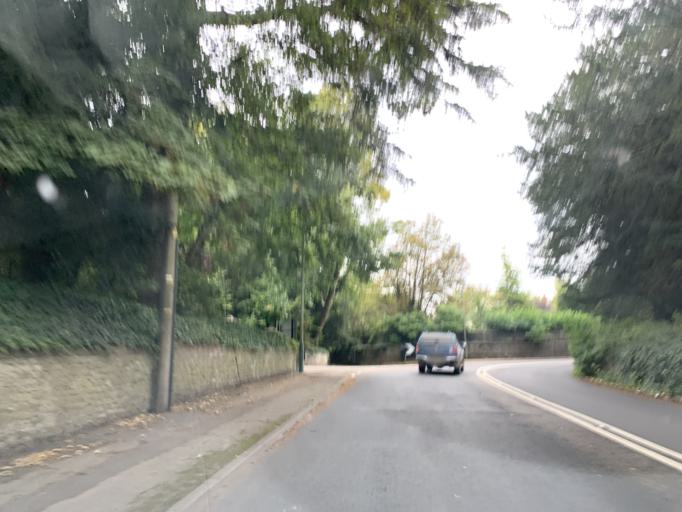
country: GB
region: England
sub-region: Wiltshire
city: Bishopstrow
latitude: 51.1965
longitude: -2.1488
